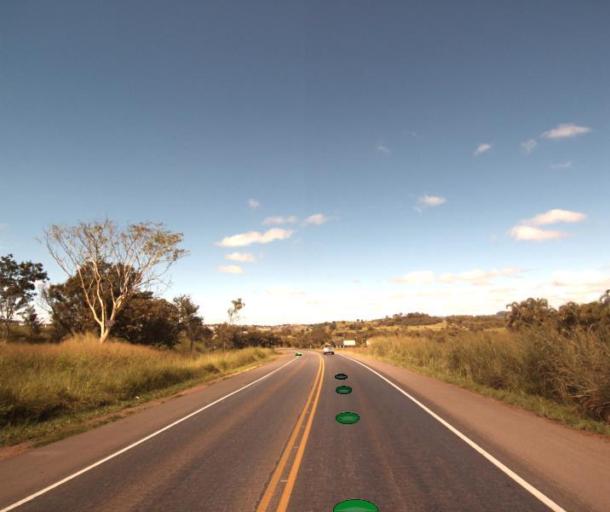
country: BR
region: Goias
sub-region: Rialma
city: Rialma
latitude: -15.2891
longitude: -49.5673
